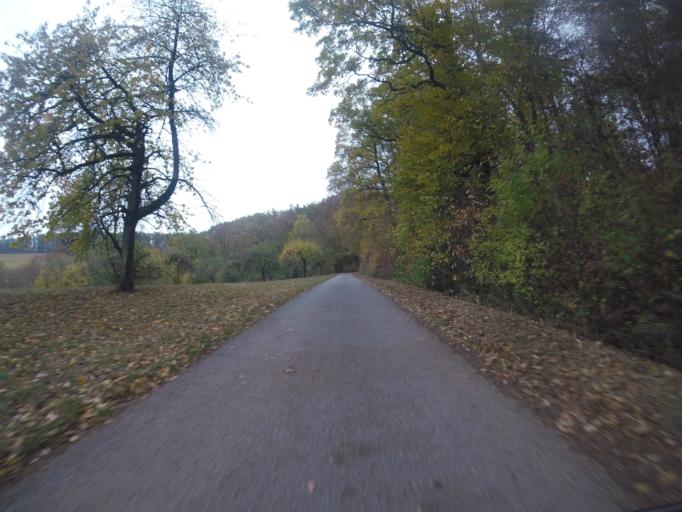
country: DE
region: Baden-Wuerttemberg
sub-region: Regierungsbezirk Stuttgart
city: Grossbottwar
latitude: 48.9810
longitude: 9.3099
